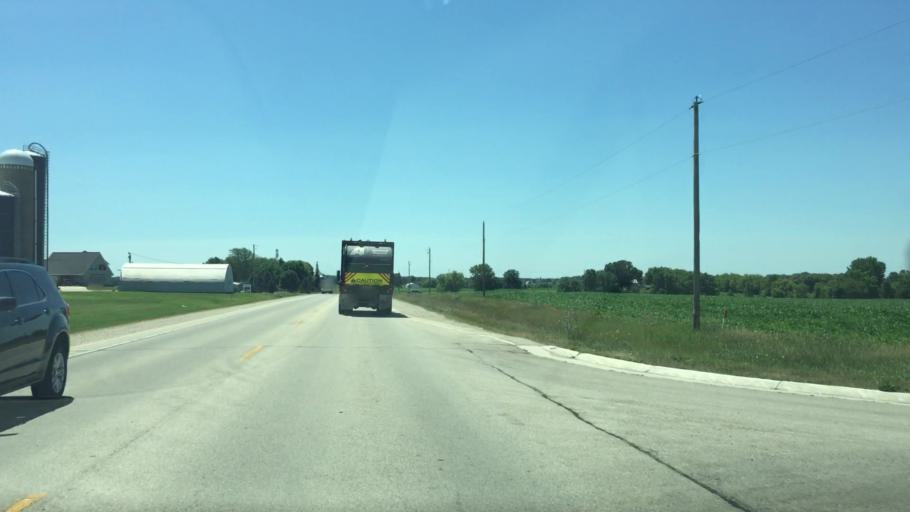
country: US
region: Wisconsin
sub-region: Calumet County
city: Hilbert
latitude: 44.0875
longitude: -88.1636
